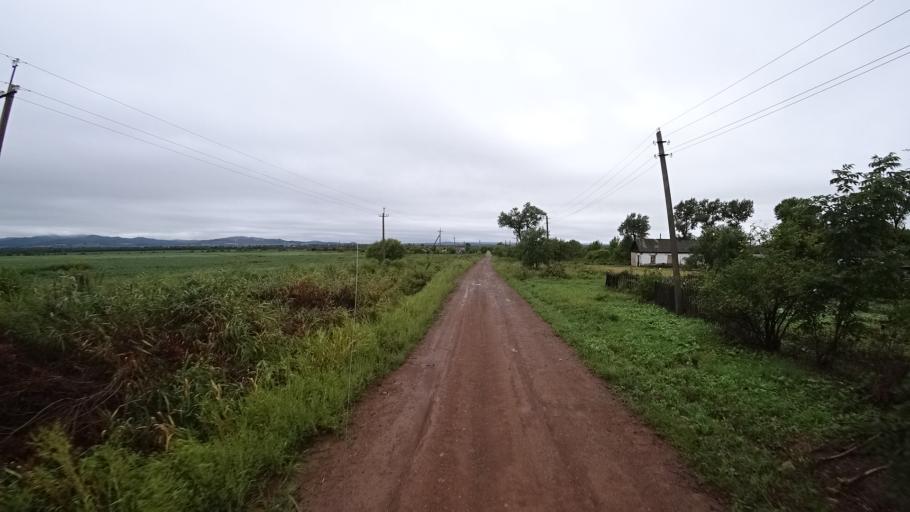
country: RU
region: Primorskiy
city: Monastyrishche
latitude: 44.2339
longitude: 132.4647
